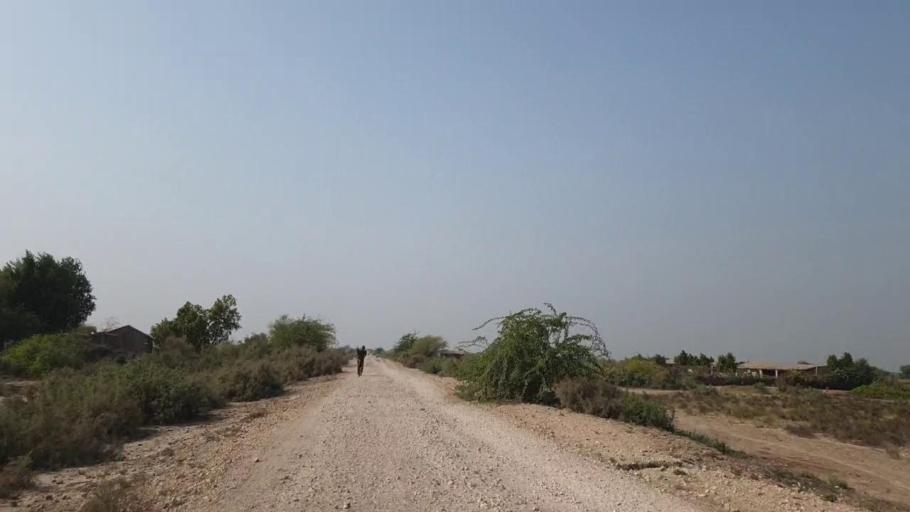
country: PK
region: Sindh
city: Kario
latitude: 24.9370
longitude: 68.5499
